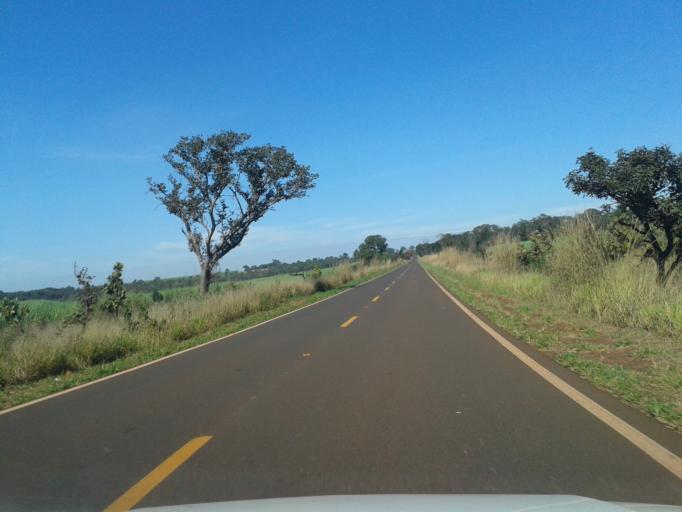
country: BR
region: Minas Gerais
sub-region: Ituiutaba
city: Ituiutaba
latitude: -19.0946
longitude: -49.7662
